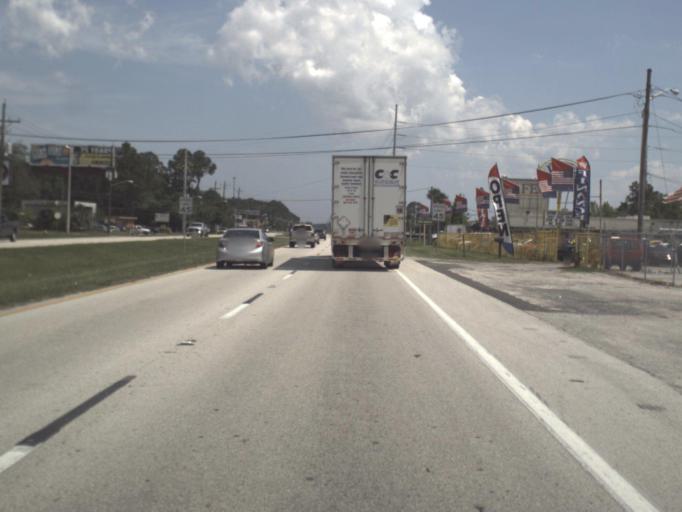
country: US
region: Florida
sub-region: Duval County
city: Jacksonville
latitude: 30.2629
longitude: -81.6162
